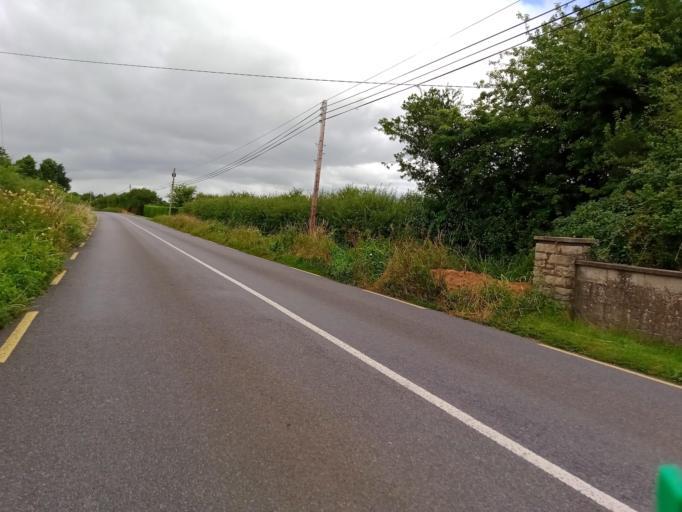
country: IE
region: Leinster
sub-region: Kilkenny
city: Callan
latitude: 52.5593
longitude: -7.4098
